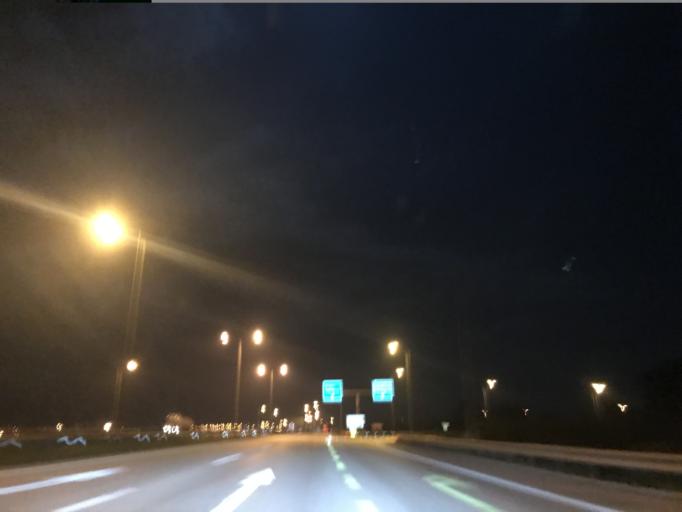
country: TR
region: Hatay
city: Mahmutlar
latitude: 36.9630
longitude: 36.1162
